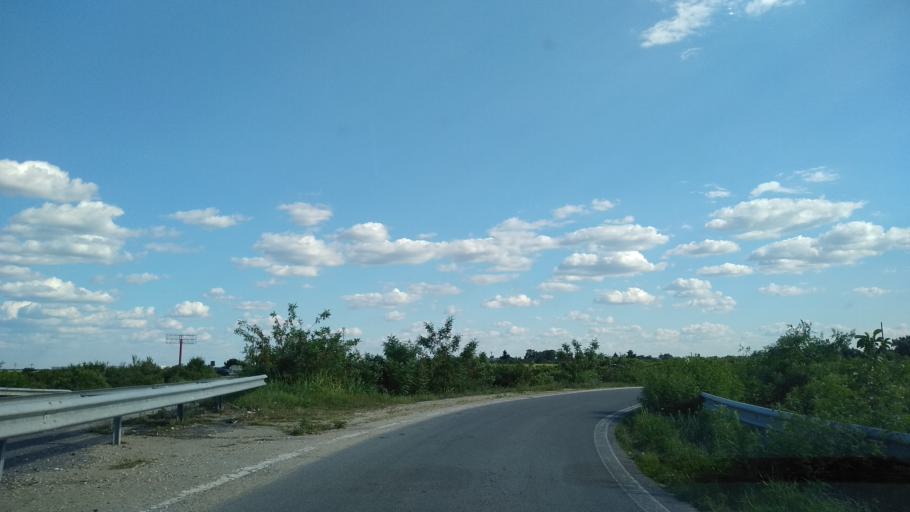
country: RO
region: Dambovita
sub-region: Comuna Petresti
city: Greci
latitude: 44.6573
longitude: 25.3400
